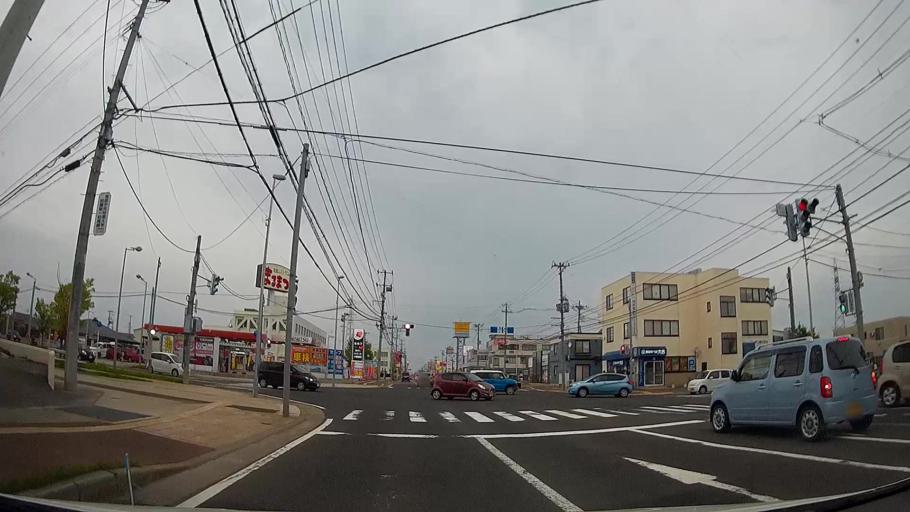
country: JP
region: Aomori
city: Aomori Shi
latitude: 40.7996
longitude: 140.7574
